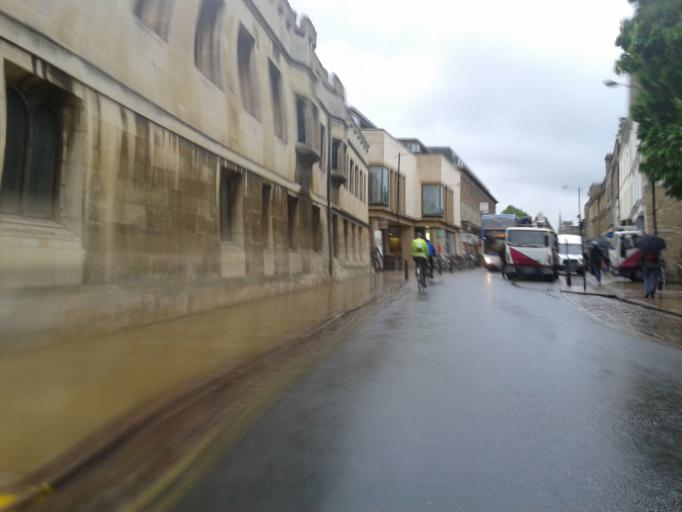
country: GB
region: England
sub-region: Cambridgeshire
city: Cambridge
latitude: 52.2052
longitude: 0.1219
